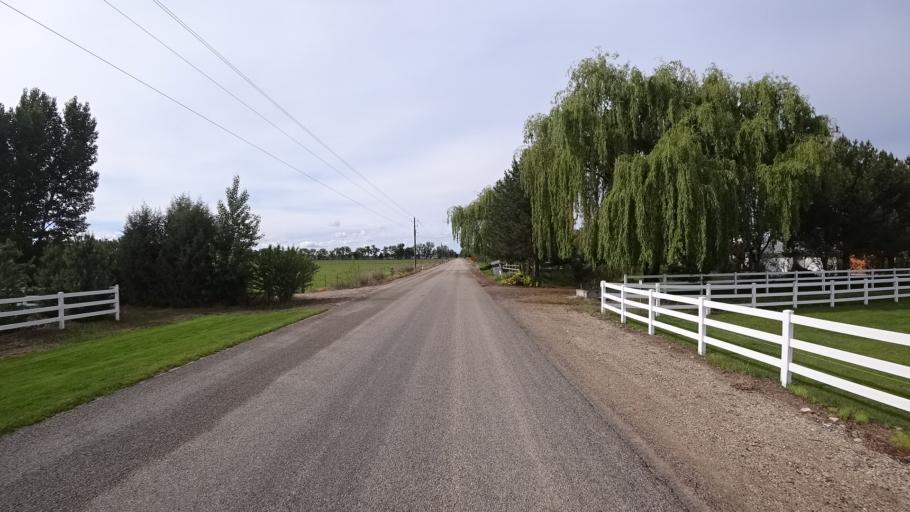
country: US
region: Idaho
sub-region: Ada County
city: Eagle
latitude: 43.7246
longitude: -116.4035
